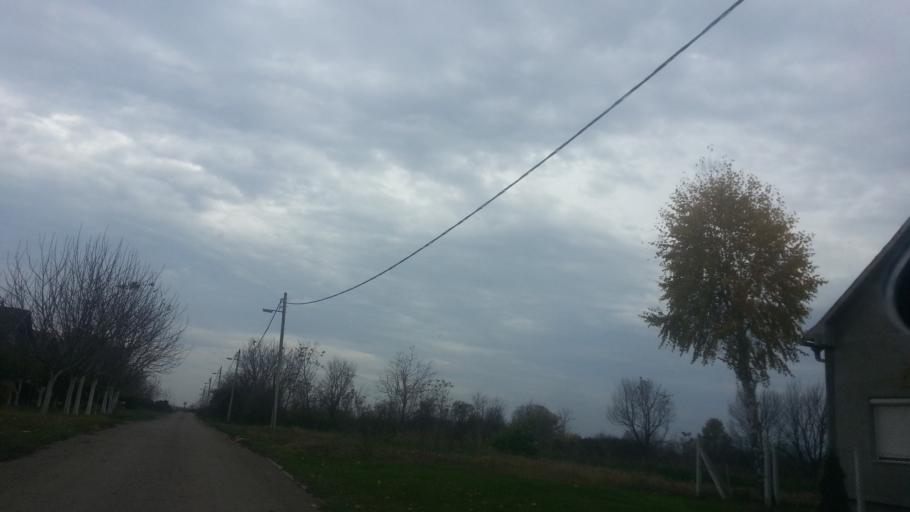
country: RS
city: Golubinci
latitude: 44.9838
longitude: 20.0485
